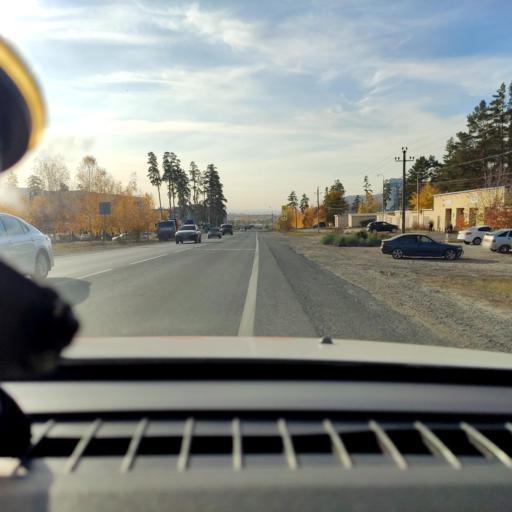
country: RU
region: Samara
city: Volzhskiy
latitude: 53.4397
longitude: 50.1240
